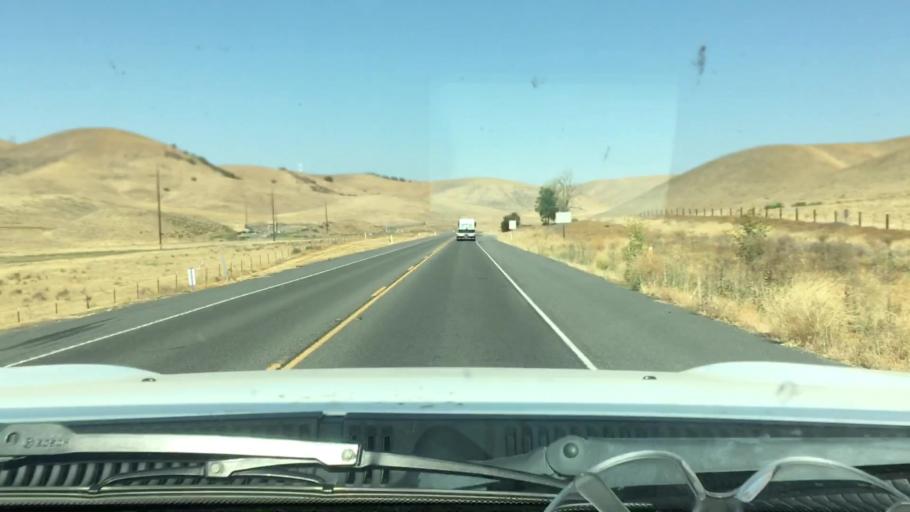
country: US
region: California
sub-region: San Luis Obispo County
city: Shandon
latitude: 35.7273
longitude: -120.1954
